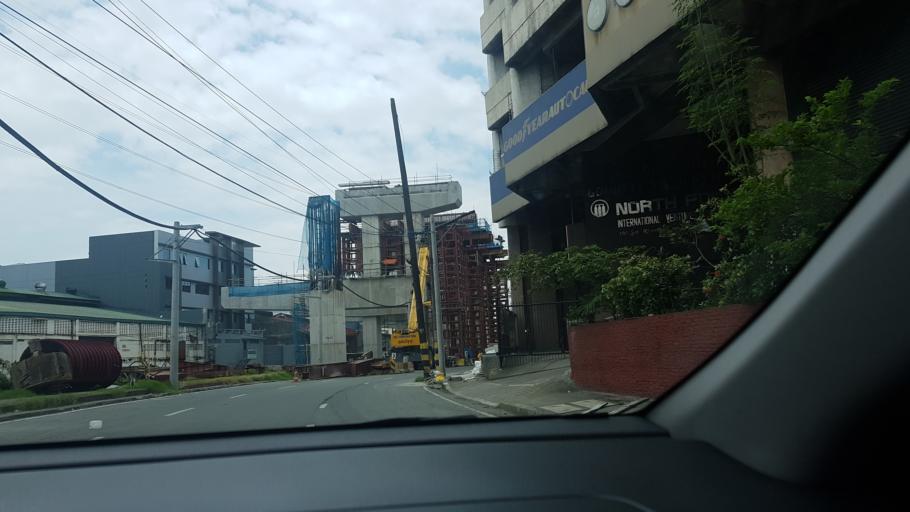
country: PH
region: Calabarzon
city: Del Monte
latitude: 14.6443
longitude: 121.0056
